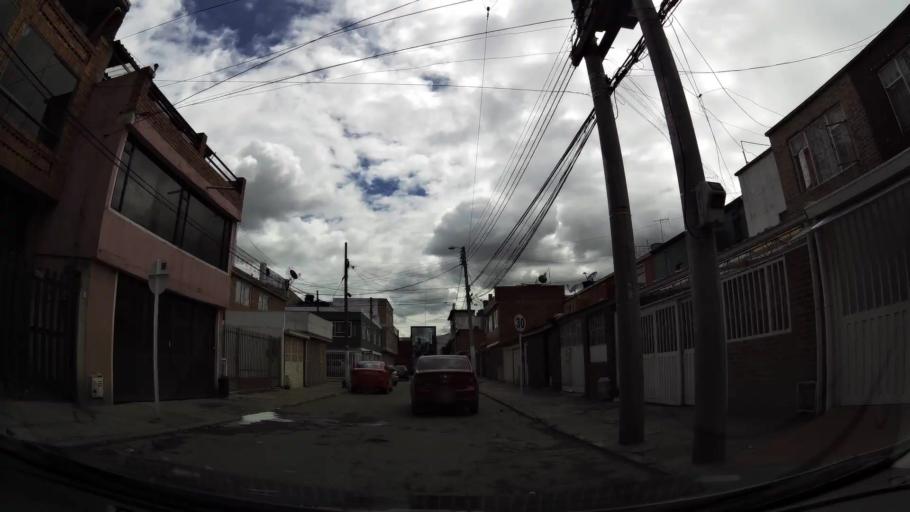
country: CO
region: Bogota D.C.
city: Barrio San Luis
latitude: 4.6939
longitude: -74.1020
